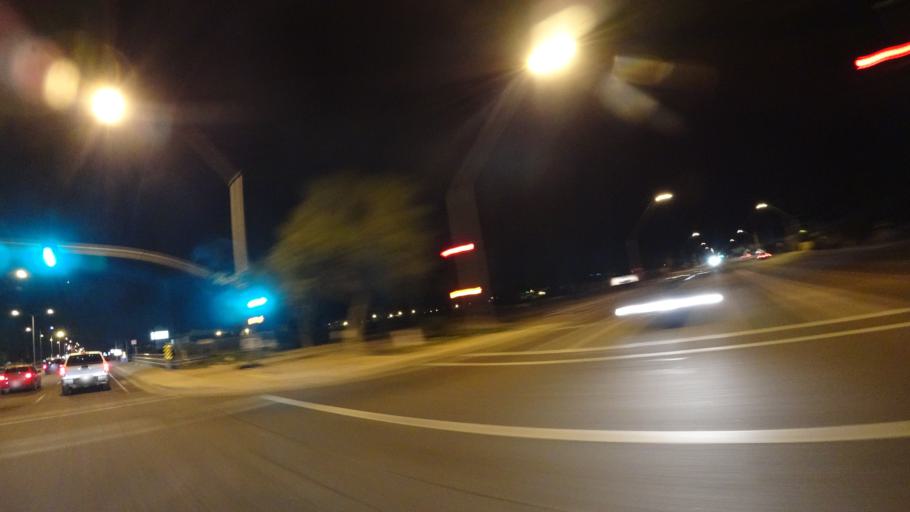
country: US
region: Arizona
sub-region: Maricopa County
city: Gilbert
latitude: 33.4157
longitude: -111.7191
